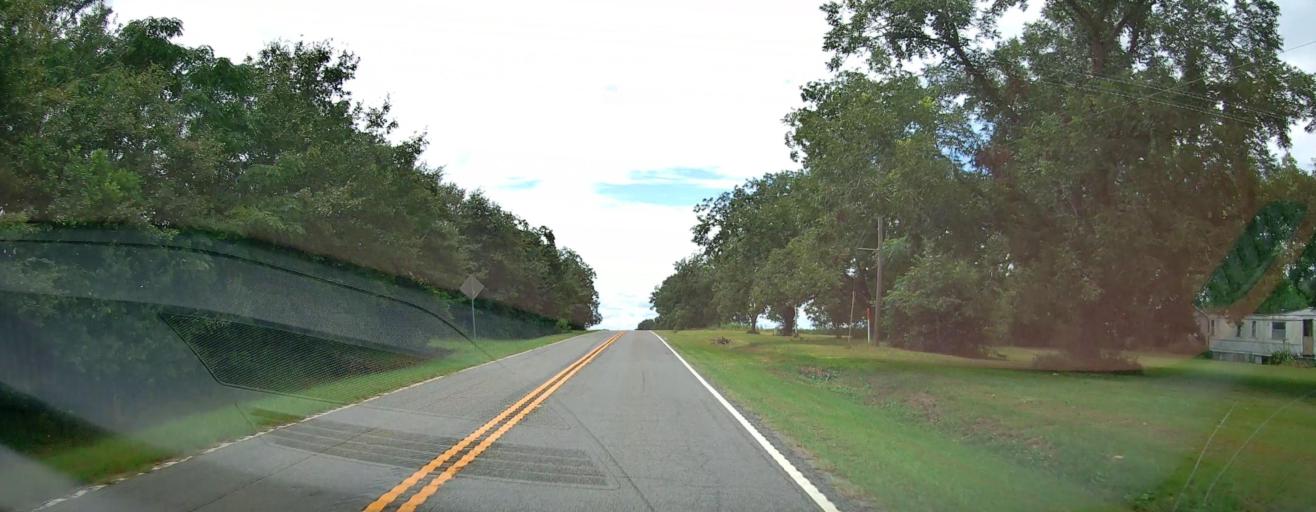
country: US
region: Georgia
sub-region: Dooly County
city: Unadilla
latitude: 32.2587
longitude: -83.7791
